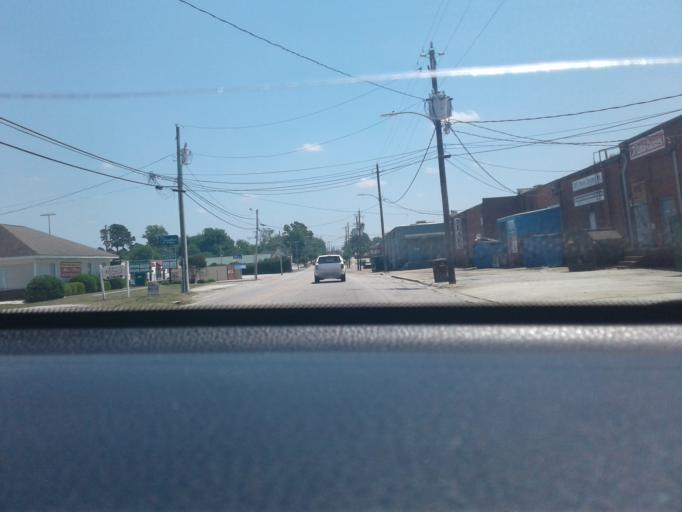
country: US
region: North Carolina
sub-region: Harnett County
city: Dunn
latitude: 35.3135
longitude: -78.6197
